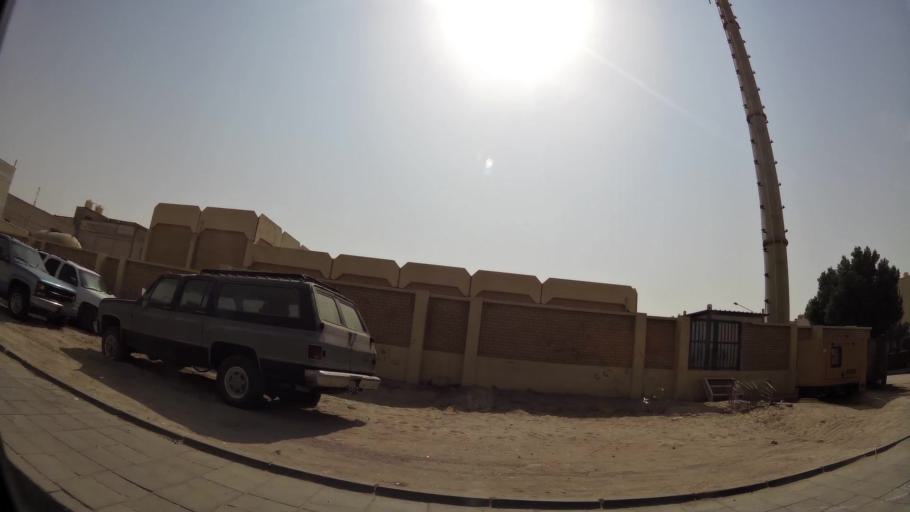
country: KW
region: Muhafazat al Jahra'
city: Al Jahra'
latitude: 29.3345
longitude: 47.6556
